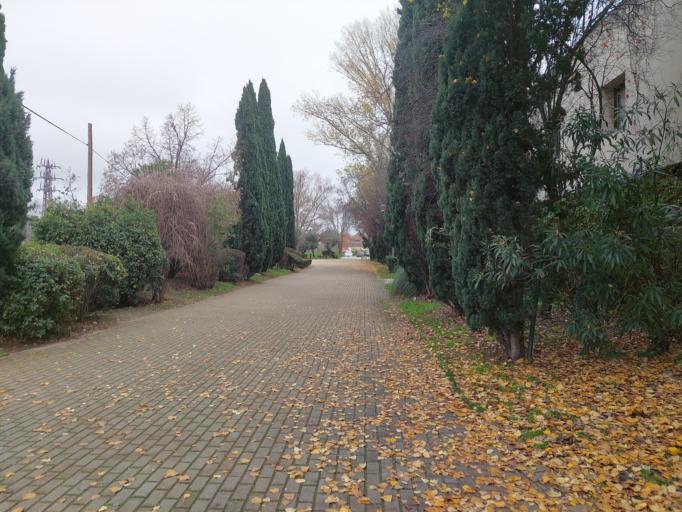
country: ES
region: Madrid
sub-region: Provincia de Madrid
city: Leganes
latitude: 40.3242
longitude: -3.7591
